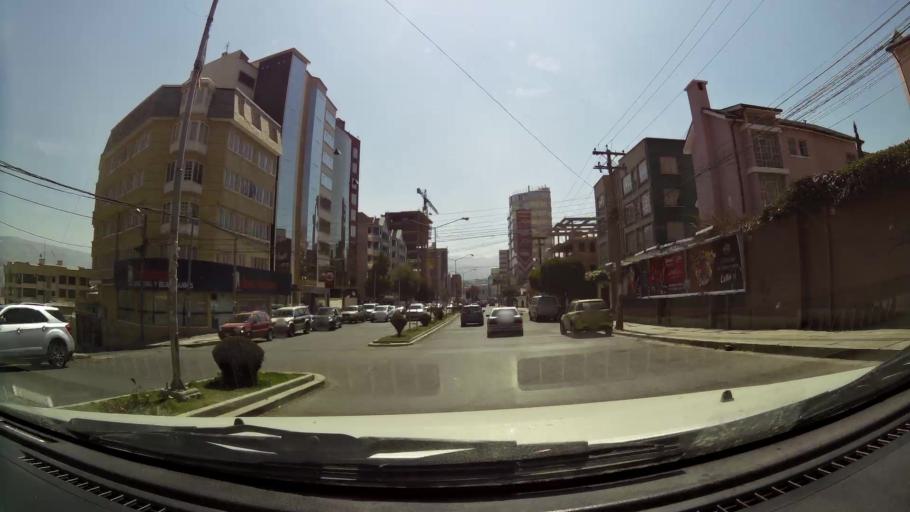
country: BO
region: La Paz
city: La Paz
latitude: -16.5466
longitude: -68.0764
